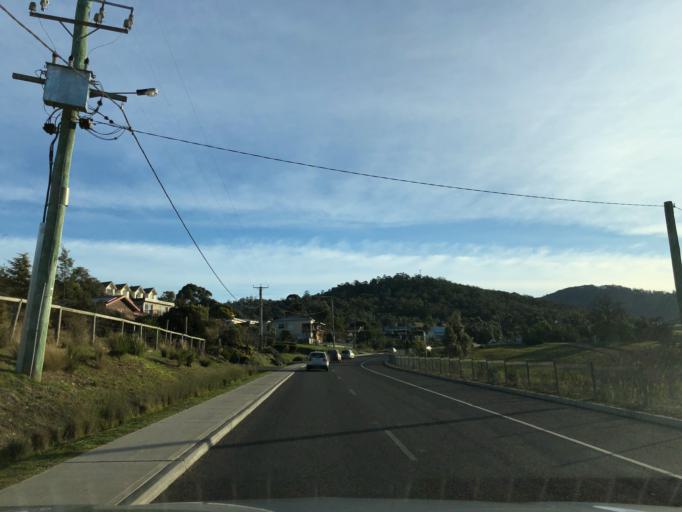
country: AU
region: Tasmania
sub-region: Kingborough
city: Kettering
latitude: -43.1285
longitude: 147.2503
